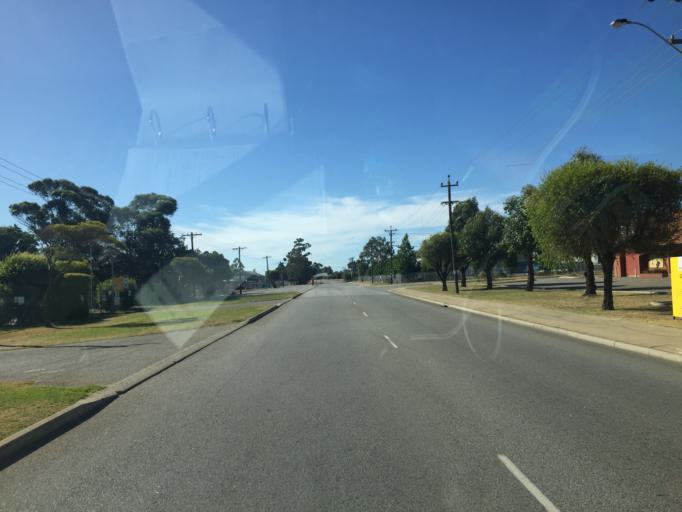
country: AU
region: Western Australia
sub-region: Gosnells
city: Maddington
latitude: -32.0431
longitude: 115.9867
